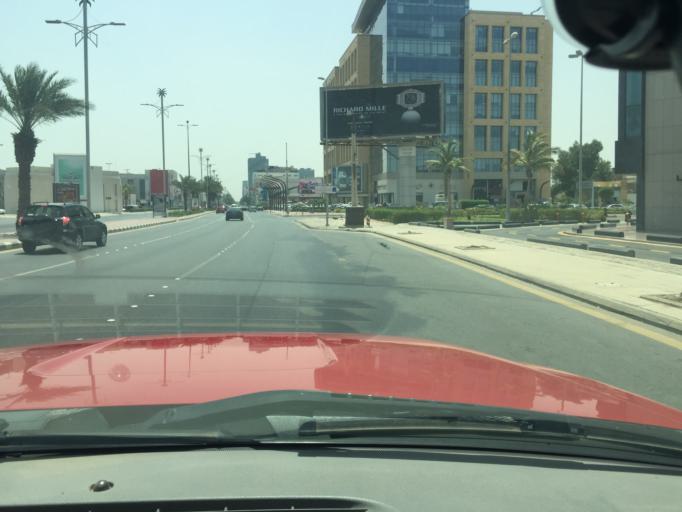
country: SA
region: Makkah
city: Jeddah
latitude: 21.5494
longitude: 39.1517
